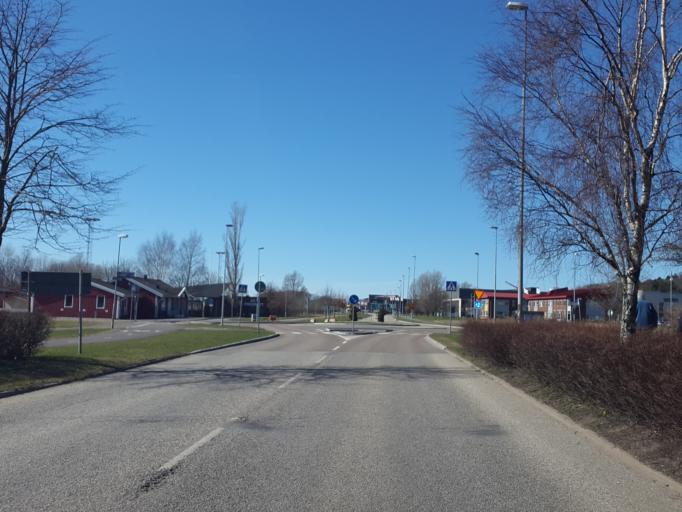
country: SE
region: Vaestra Goetaland
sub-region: Molndal
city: Moelndal
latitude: 57.6472
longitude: 11.9951
